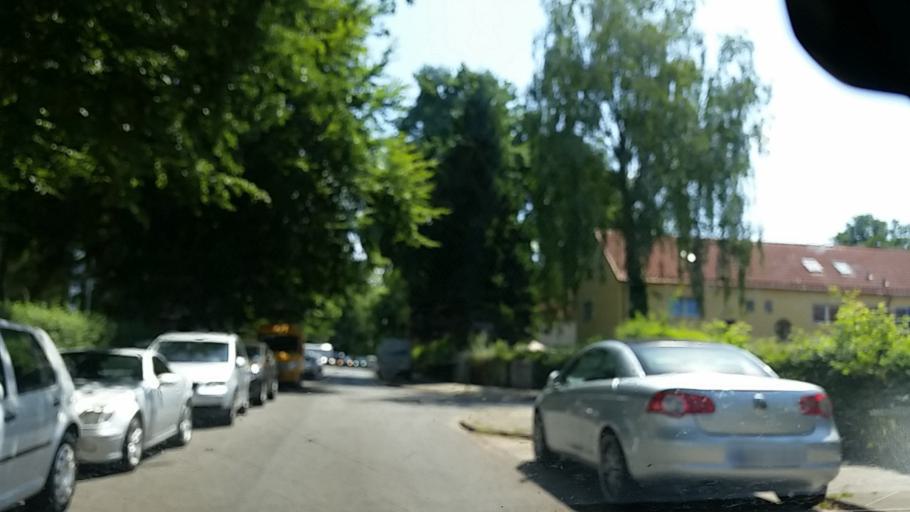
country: DE
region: Schleswig-Holstein
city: Halstenbek
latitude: 53.5819
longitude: 9.8072
